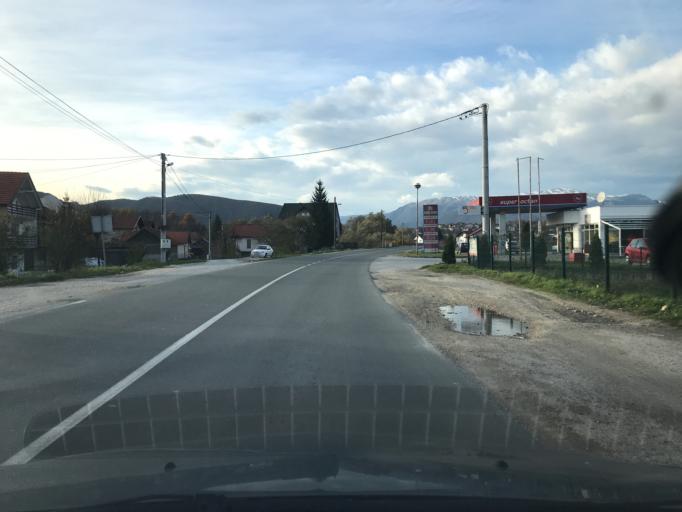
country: BA
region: Federation of Bosnia and Herzegovina
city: Vitez
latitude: 44.1661
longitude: 17.7708
